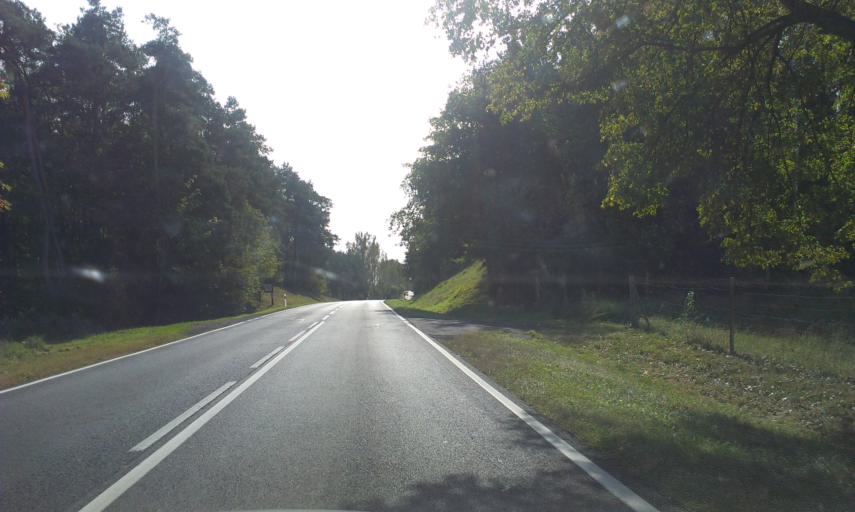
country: PL
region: Greater Poland Voivodeship
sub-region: Powiat zlotowski
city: Okonek
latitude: 53.5536
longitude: 16.8385
